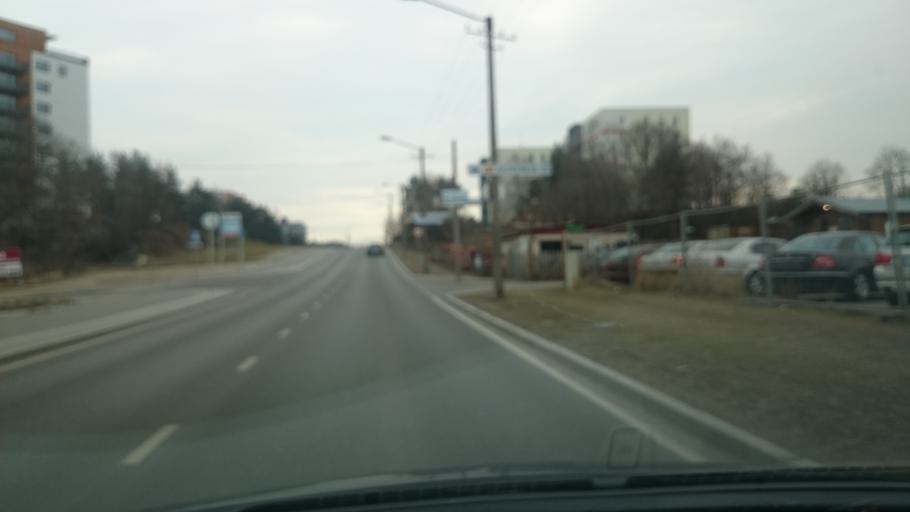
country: EE
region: Harju
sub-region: Saue vald
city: Laagri
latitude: 59.3989
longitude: 24.6457
